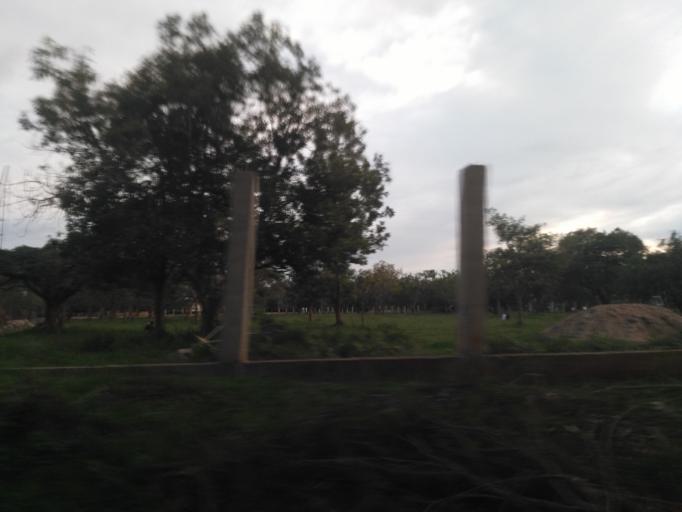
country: UG
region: Eastern Region
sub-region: Jinja District
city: Jinja
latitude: 0.4267
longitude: 33.1992
